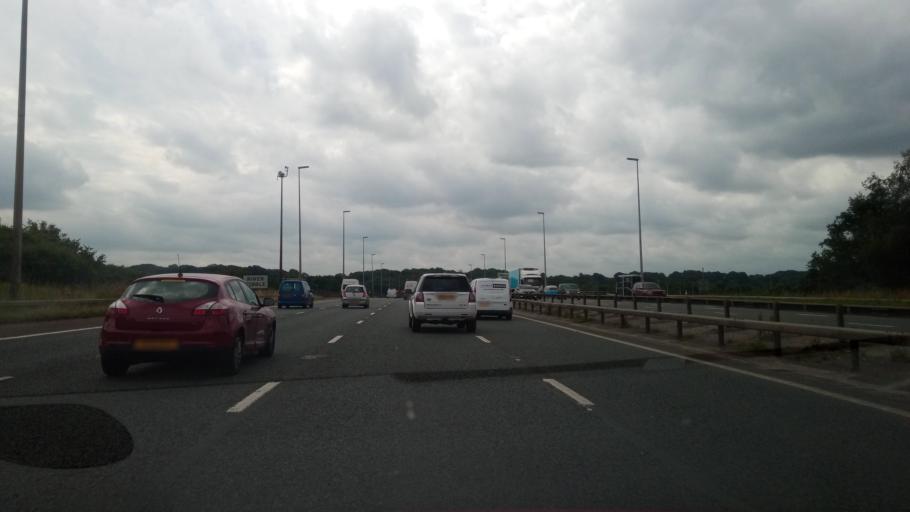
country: GB
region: England
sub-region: Lancashire
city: Goosnargh
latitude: 53.7672
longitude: -2.6363
